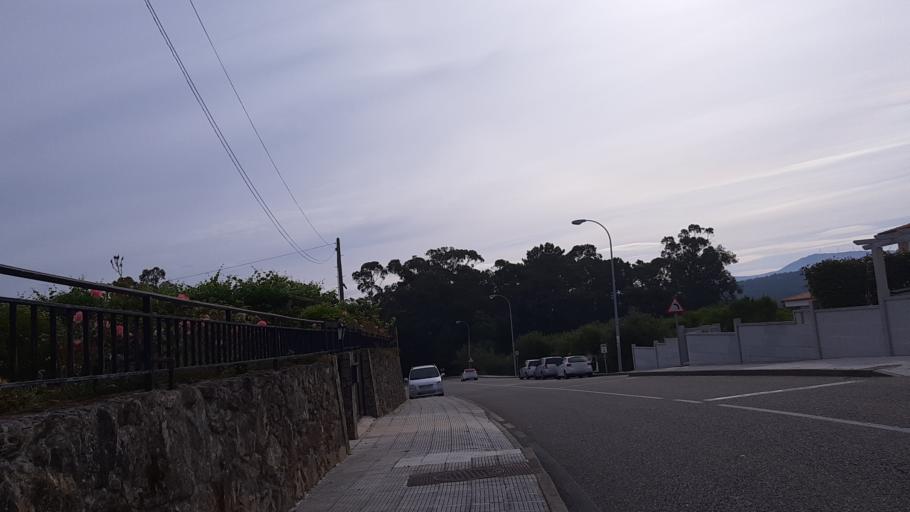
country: ES
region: Galicia
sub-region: Provincia de Pontevedra
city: O Rosal
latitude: 41.9276
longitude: -8.8378
